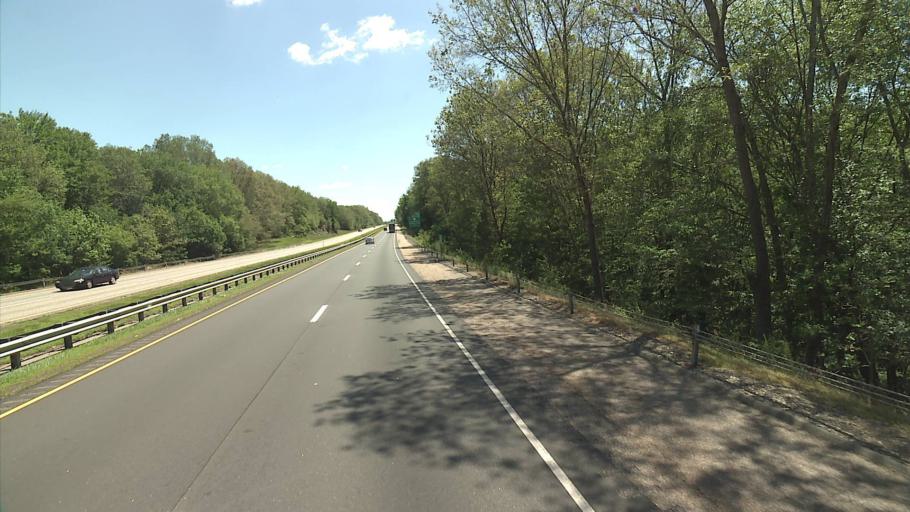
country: US
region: Connecticut
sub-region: New London County
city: Lisbon
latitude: 41.5902
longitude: -72.0122
